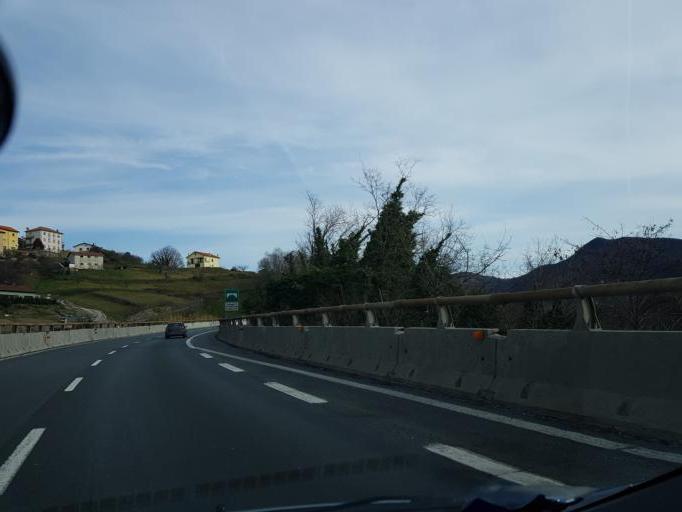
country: IT
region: Liguria
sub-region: Provincia di Genova
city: Pedemonte
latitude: 44.5044
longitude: 8.9197
